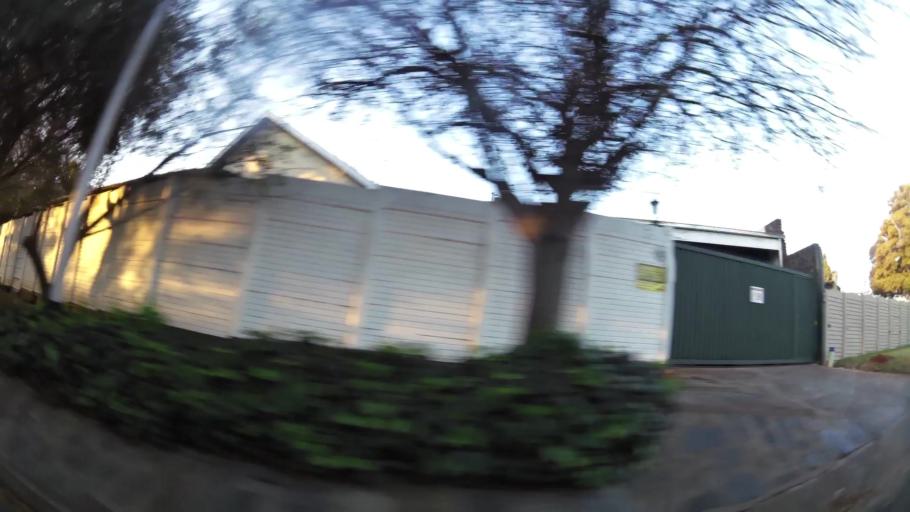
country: ZA
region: Gauteng
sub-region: City of Johannesburg Metropolitan Municipality
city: Roodepoort
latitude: -26.1571
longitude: 27.8879
